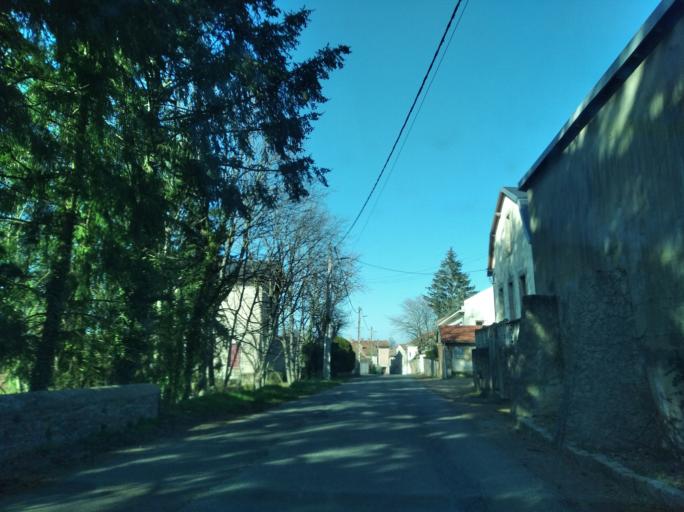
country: FR
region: Auvergne
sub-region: Departement de l'Allier
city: Le Mayet-de-Montagne
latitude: 46.1120
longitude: 3.6828
